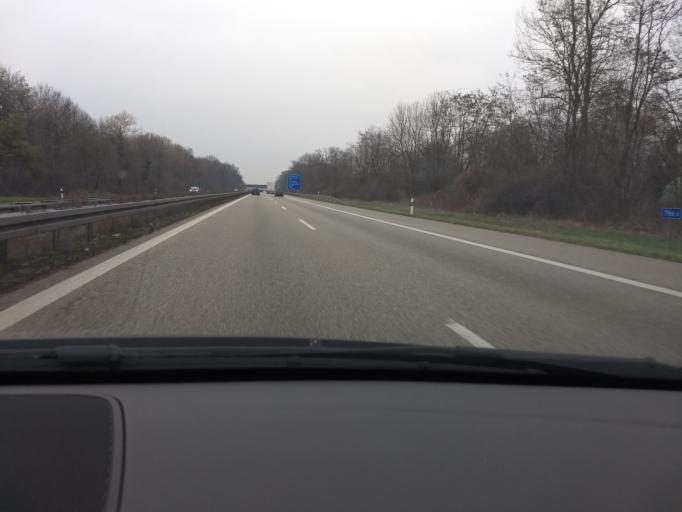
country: DE
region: Baden-Wuerttemberg
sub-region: Freiburg Region
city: Neuenburg am Rhein
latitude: 47.8077
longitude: 7.5485
